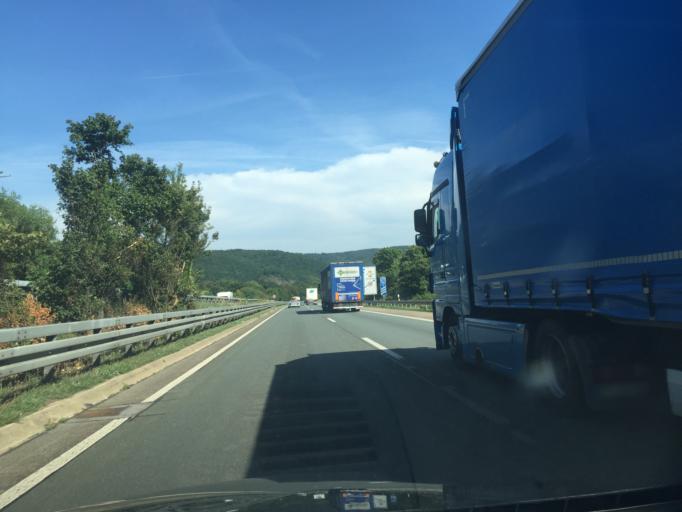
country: DE
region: Hesse
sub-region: Regierungsbezirk Giessen
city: Merkenbach
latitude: 50.6633
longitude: 8.3047
